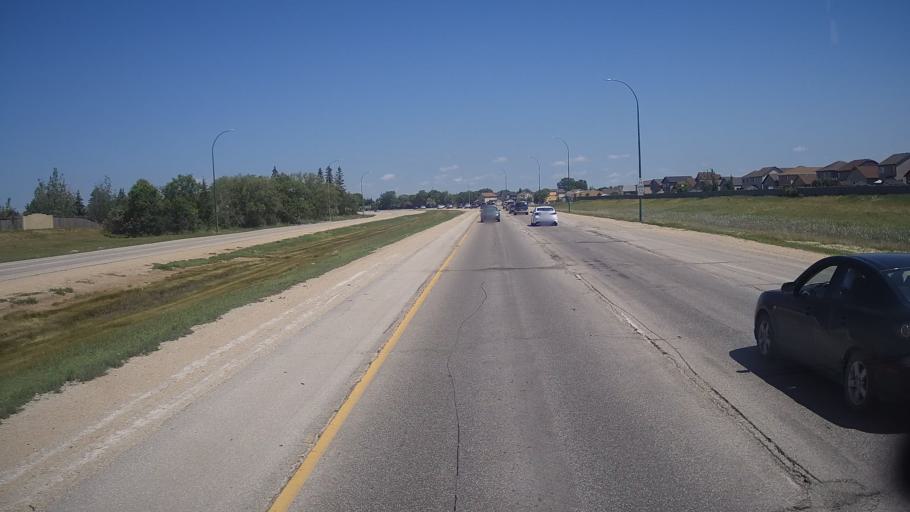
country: CA
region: Manitoba
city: Winnipeg
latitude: 49.9157
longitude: -97.0528
